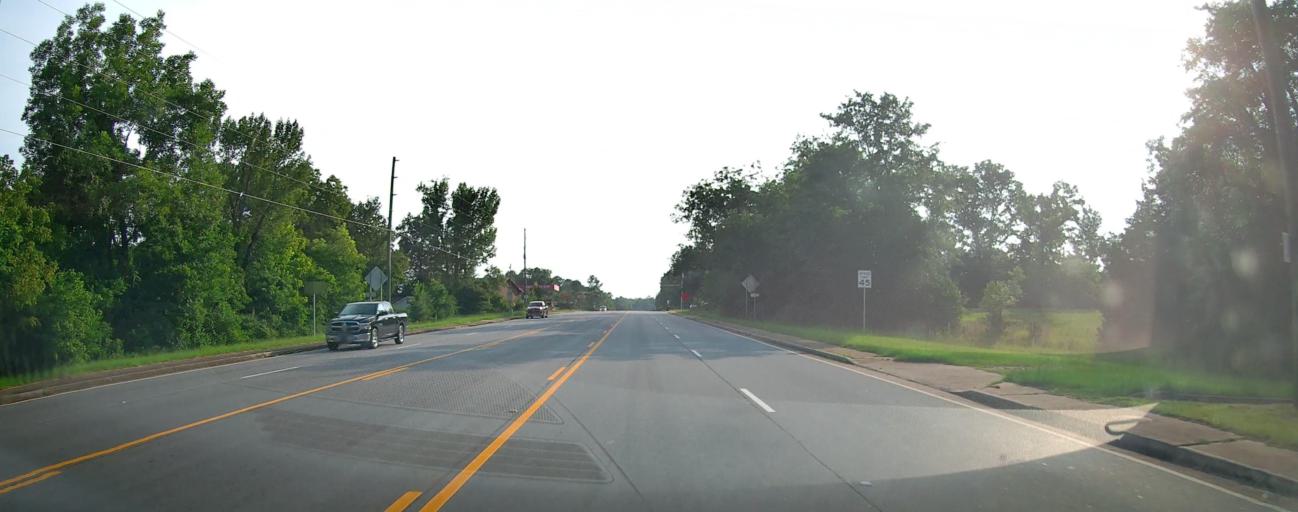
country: US
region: Georgia
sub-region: Talbot County
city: Talbotton
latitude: 32.5783
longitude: -84.5536
